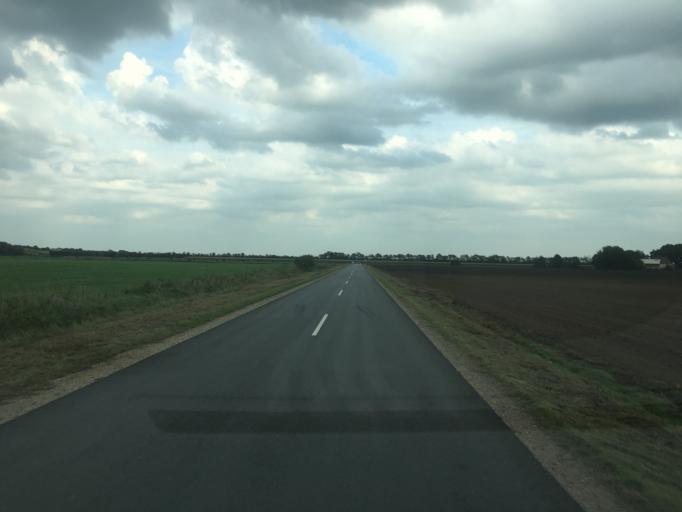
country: DK
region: South Denmark
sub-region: Tonder Kommune
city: Logumkloster
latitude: 55.0612
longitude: 9.0602
